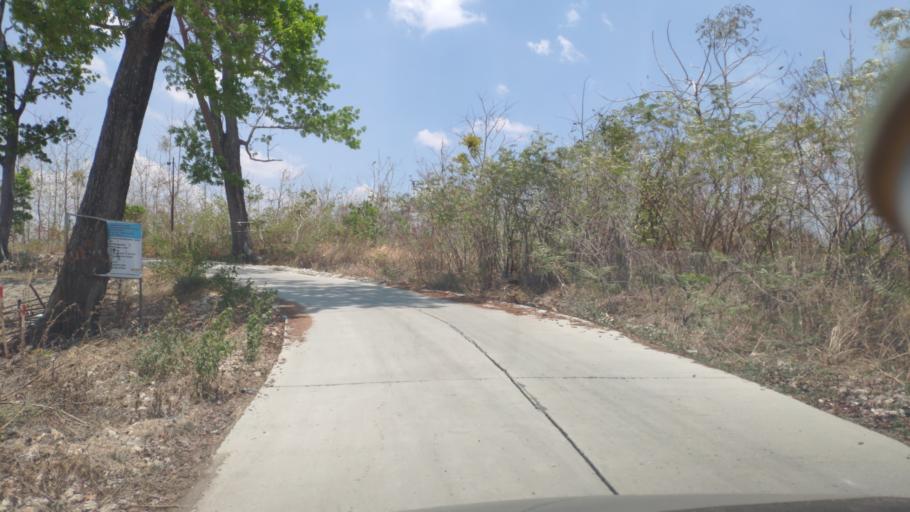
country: ID
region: Central Java
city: Randublatung
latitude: -7.2774
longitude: 111.3742
